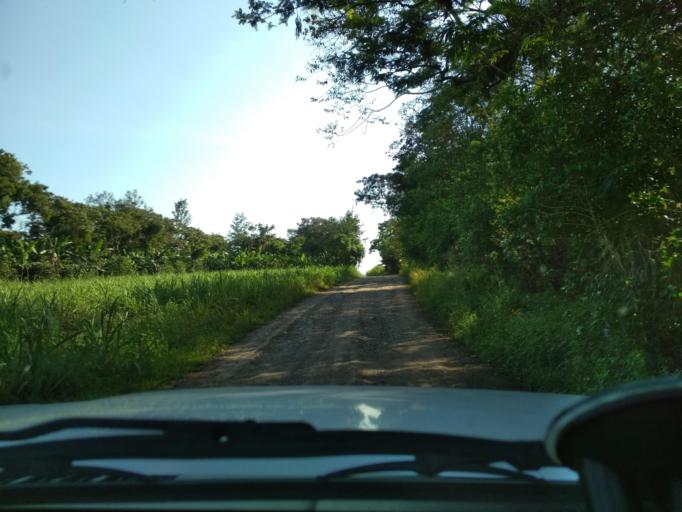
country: MX
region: Veracruz
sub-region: Chocaman
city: San Jose Neria
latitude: 18.9862
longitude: -97.0057
